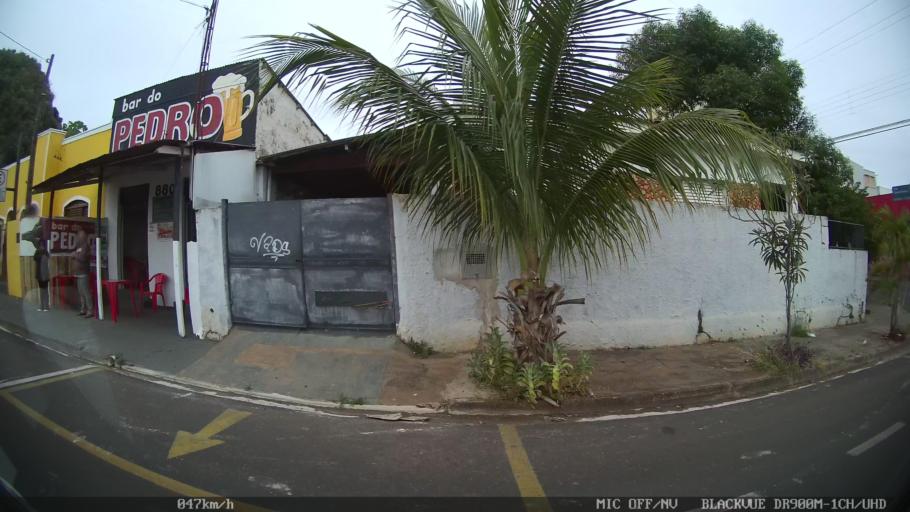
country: BR
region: Sao Paulo
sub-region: Sao Jose Do Rio Preto
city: Sao Jose do Rio Preto
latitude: -20.8379
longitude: -49.3861
